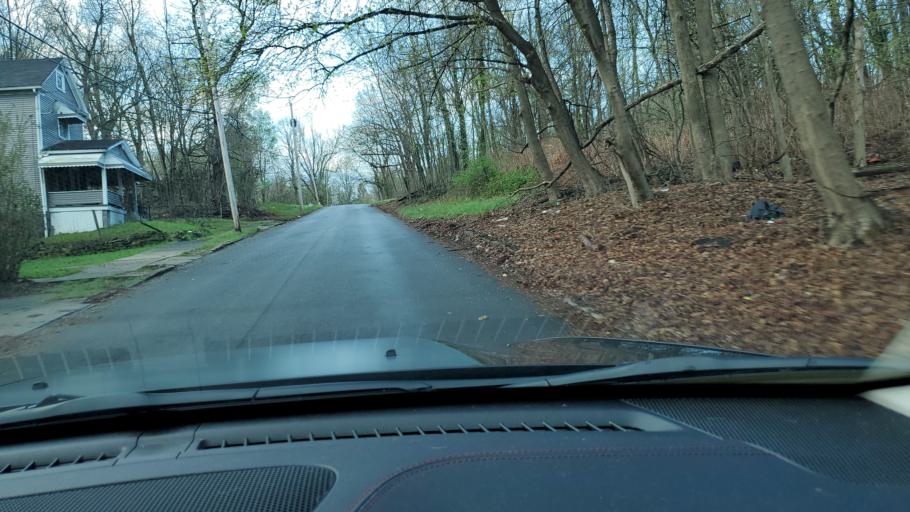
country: US
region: Ohio
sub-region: Mahoning County
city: Youngstown
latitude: 41.0968
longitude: -80.6650
